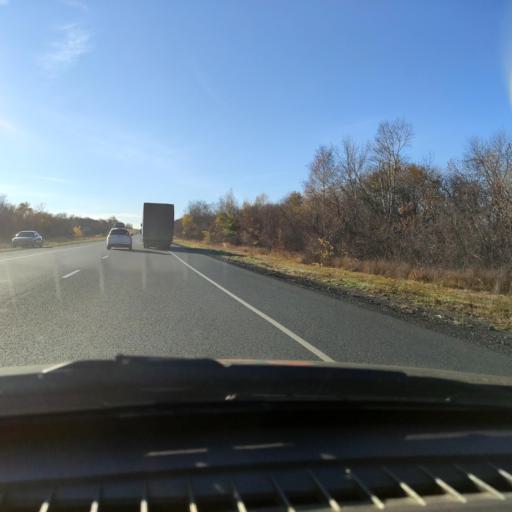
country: RU
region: Samara
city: Obsharovka
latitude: 53.2314
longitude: 48.9180
